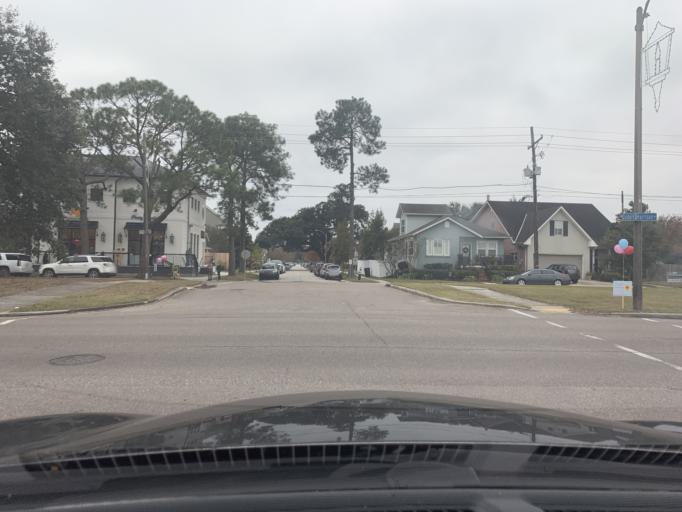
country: US
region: Louisiana
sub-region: Jefferson Parish
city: Metairie
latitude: 30.0052
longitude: -90.1114
